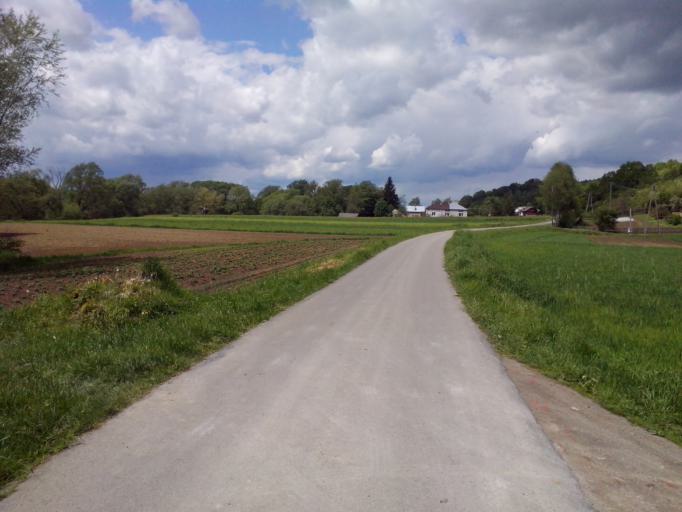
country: PL
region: Subcarpathian Voivodeship
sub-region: Powiat strzyzowski
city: Strzyzow
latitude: 49.8409
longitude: 21.8310
